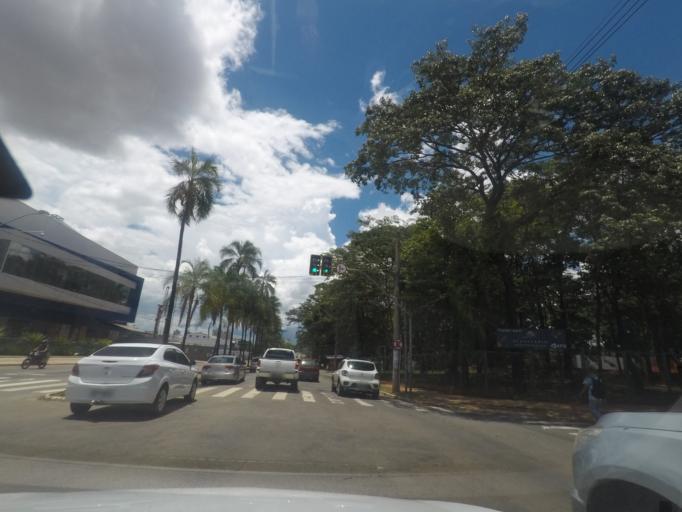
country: BR
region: Goias
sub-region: Goiania
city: Goiania
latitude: -16.6624
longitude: -49.2544
